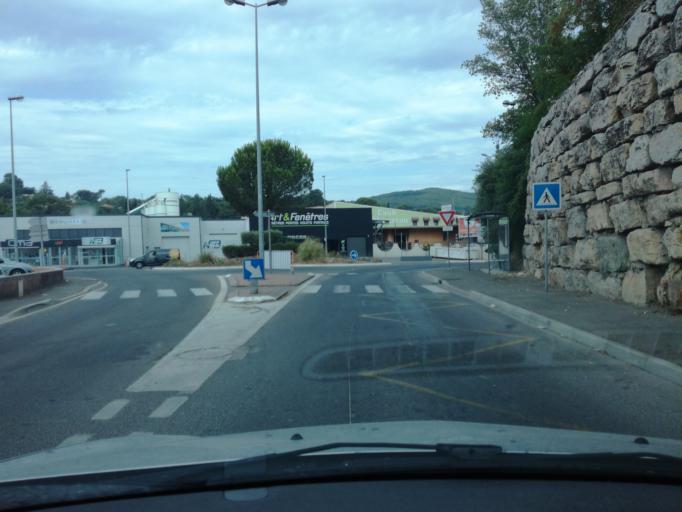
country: FR
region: Provence-Alpes-Cote d'Azur
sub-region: Departement du Var
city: Draguignan
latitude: 43.5279
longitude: 6.4496
